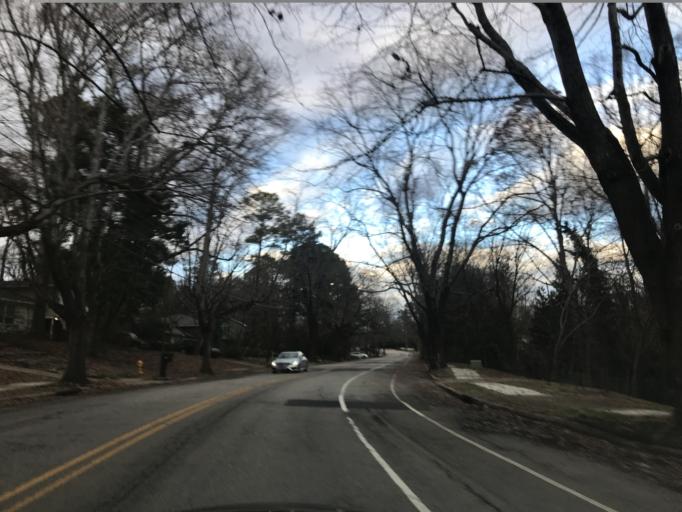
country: US
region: North Carolina
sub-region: Wake County
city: West Raleigh
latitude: 35.8505
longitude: -78.6609
